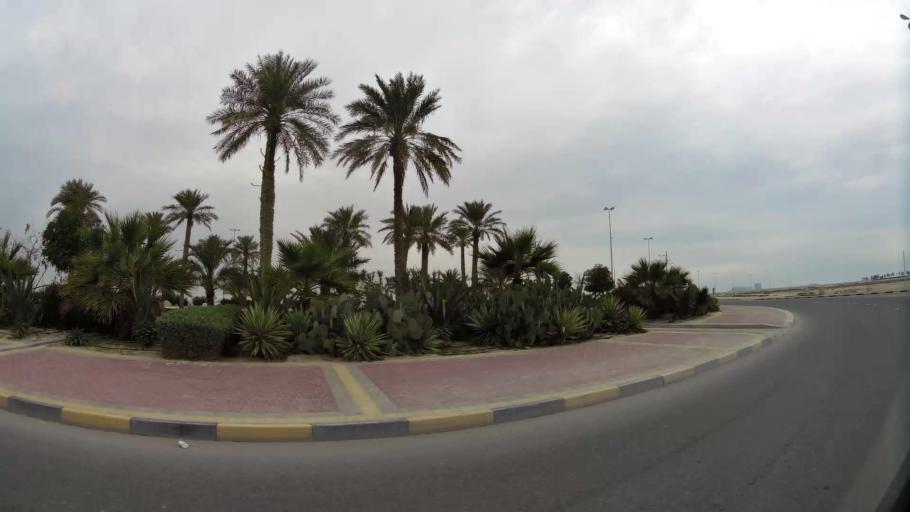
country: BH
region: Central Governorate
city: Dar Kulayb
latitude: 25.8454
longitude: 50.5855
